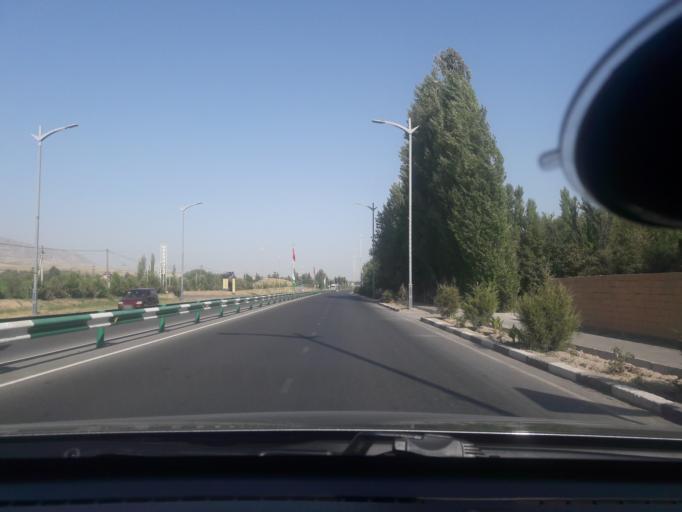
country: TJ
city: Shahrinav
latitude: 38.5764
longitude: 68.3390
